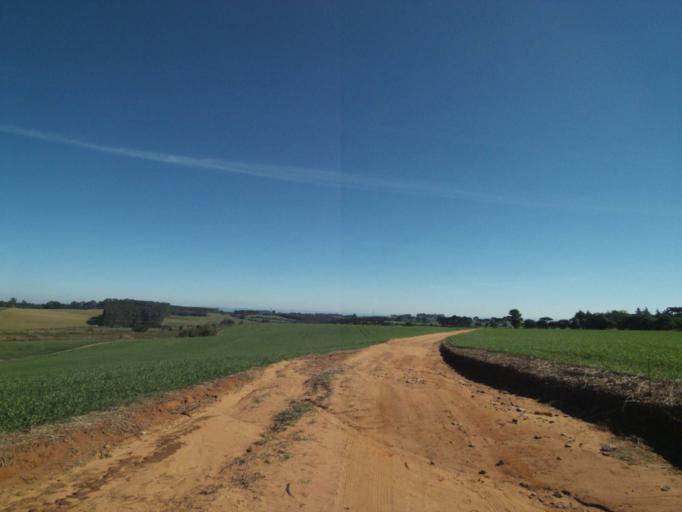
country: BR
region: Parana
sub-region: Tibagi
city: Tibagi
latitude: -24.5987
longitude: -50.2423
